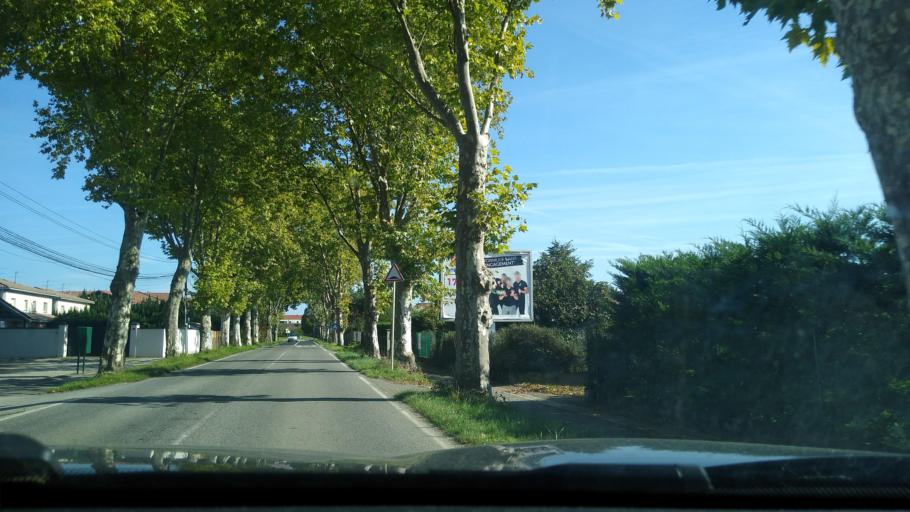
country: FR
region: Midi-Pyrenees
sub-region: Departement de la Haute-Garonne
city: Mondonville
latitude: 43.6729
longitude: 1.2810
